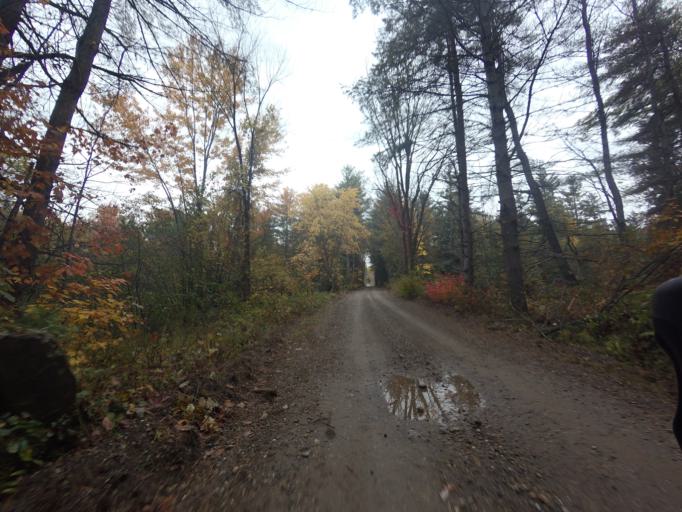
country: CA
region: Ontario
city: Renfrew
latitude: 45.1829
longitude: -76.6848
